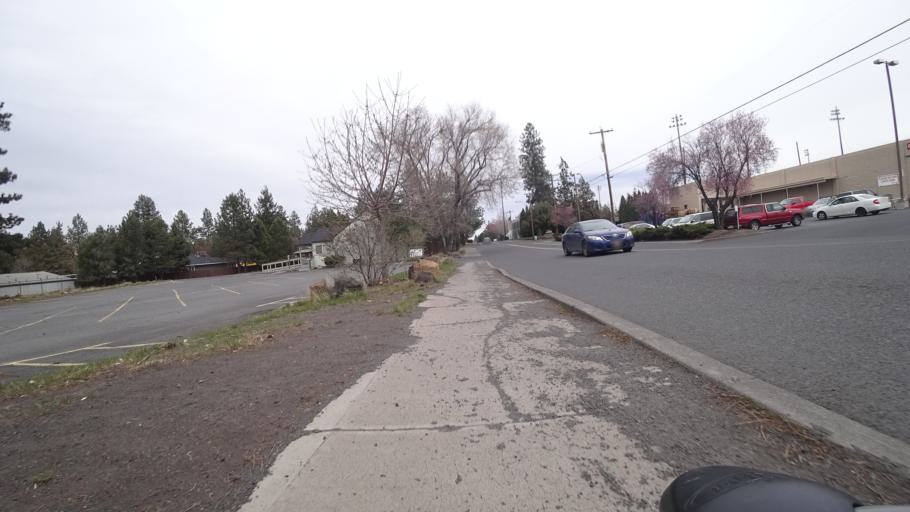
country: US
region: Oregon
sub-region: Deschutes County
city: Bend
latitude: 44.0443
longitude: -121.3016
